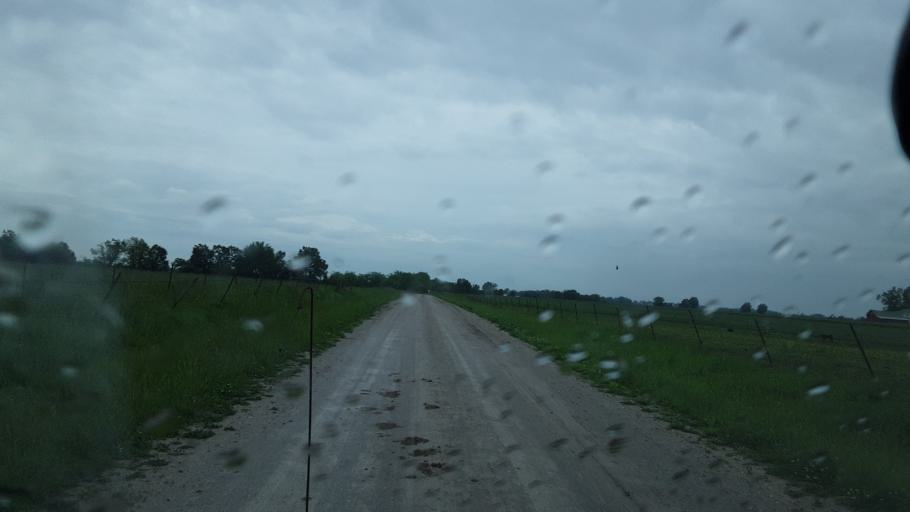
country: US
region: Missouri
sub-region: Randolph County
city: Moberly
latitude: 39.3070
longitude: -92.3053
